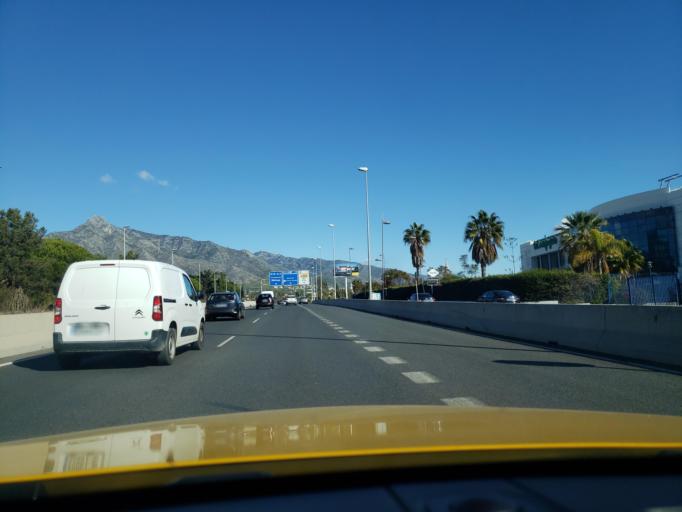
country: ES
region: Andalusia
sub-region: Provincia de Malaga
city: Marbella
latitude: 36.4907
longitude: -4.9544
